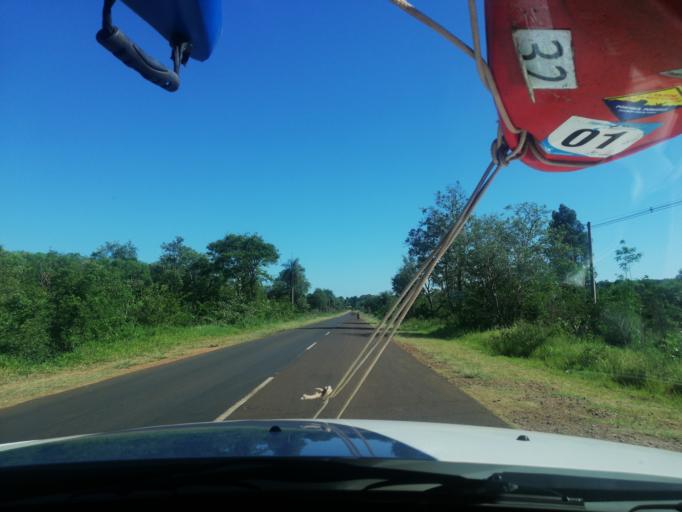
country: AR
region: Misiones
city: Santa Ana
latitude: -27.3451
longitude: -55.5840
